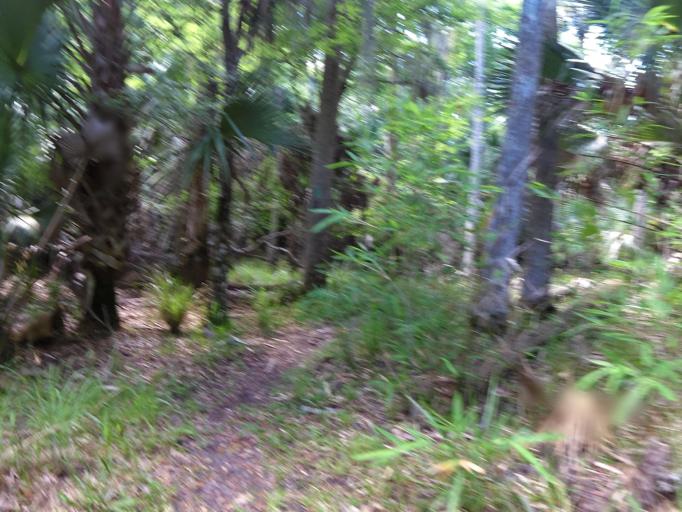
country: US
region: Florida
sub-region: Flagler County
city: Flagler Beach
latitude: 29.4211
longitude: -81.1359
